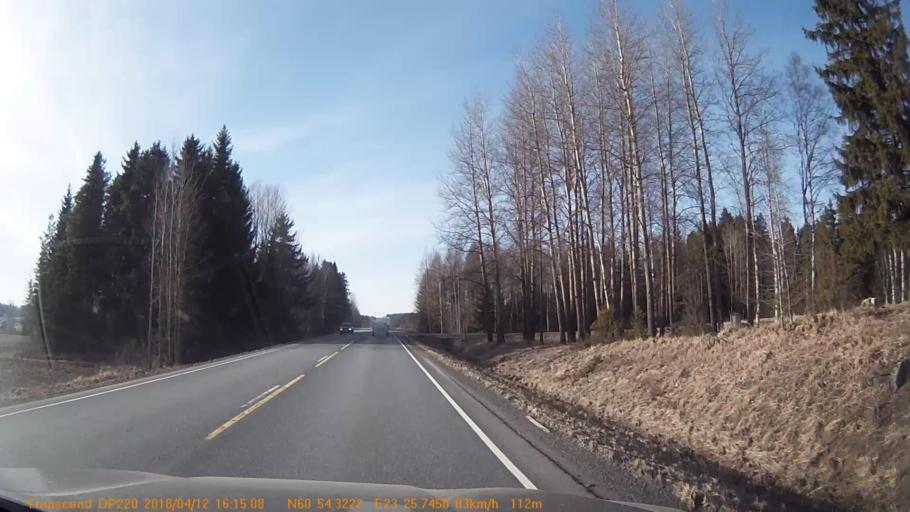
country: FI
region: Haeme
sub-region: Forssa
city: Humppila
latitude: 60.9055
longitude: 23.4288
